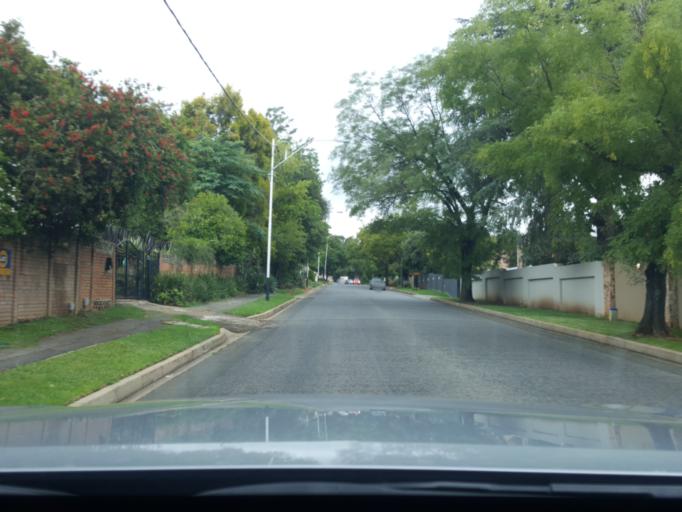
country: ZA
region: Gauteng
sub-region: City of Johannesburg Metropolitan Municipality
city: Johannesburg
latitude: -26.1301
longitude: 28.0017
